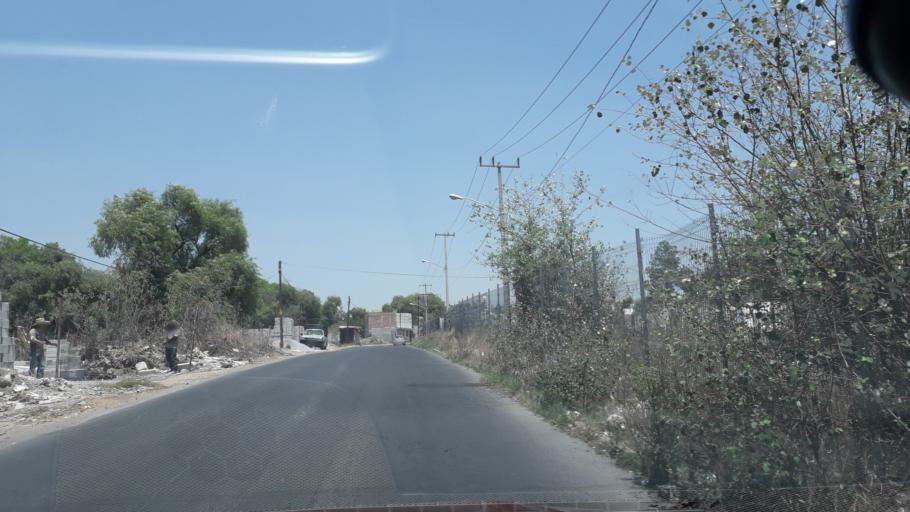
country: MX
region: Puebla
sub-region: Puebla
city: Articulo Primero Constitucional
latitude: 18.9871
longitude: -98.1850
